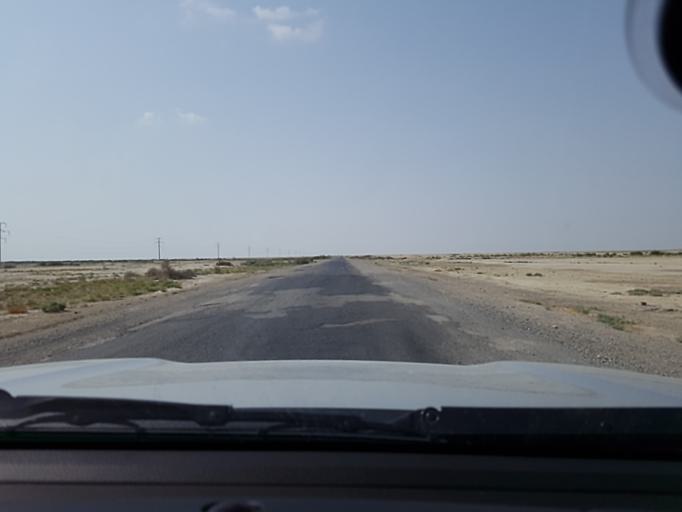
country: TM
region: Balkan
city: Gumdag
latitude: 38.9013
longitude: 54.5923
